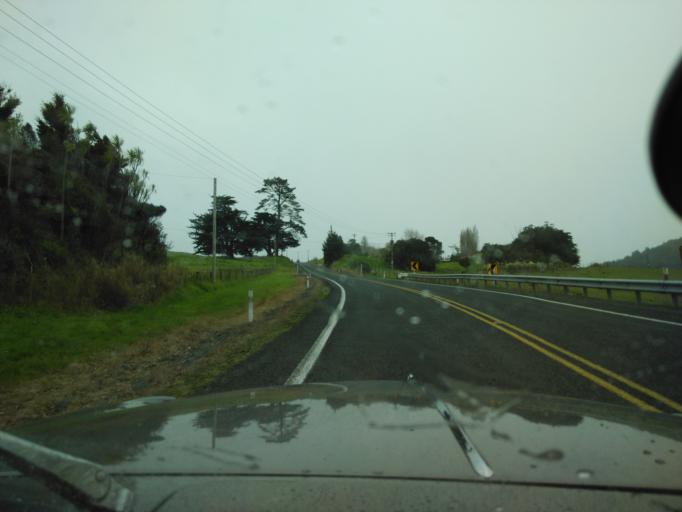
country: NZ
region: Auckland
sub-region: Auckland
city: Wellsford
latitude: -36.3937
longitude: 174.4453
